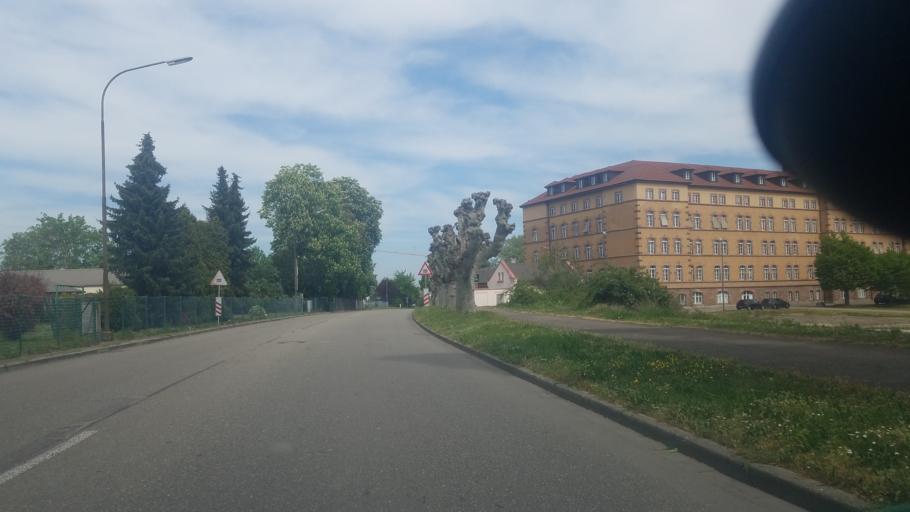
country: DE
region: Baden-Wuerttemberg
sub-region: Freiburg Region
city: Kehl
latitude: 48.5772
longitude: 7.8038
